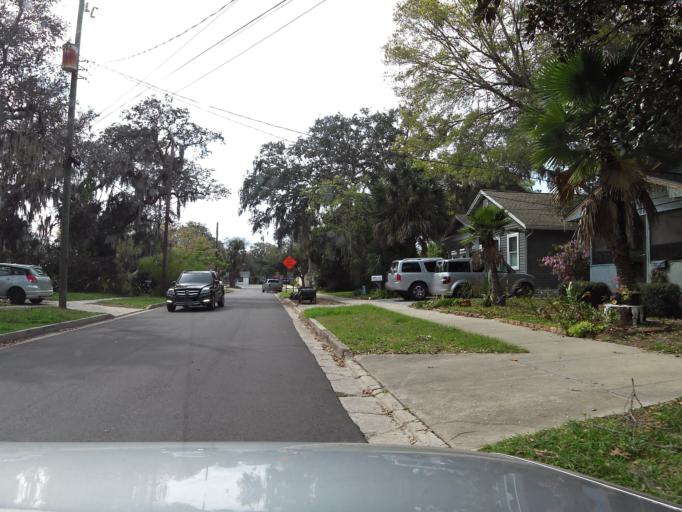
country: US
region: Florida
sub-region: Saint Johns County
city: Saint Augustine
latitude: 29.9165
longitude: -81.3212
